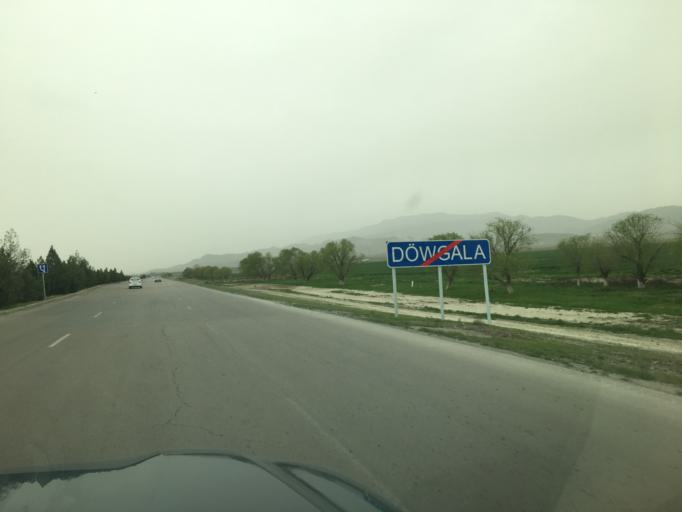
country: TM
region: Ahal
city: Baharly
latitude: 38.2985
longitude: 57.6350
